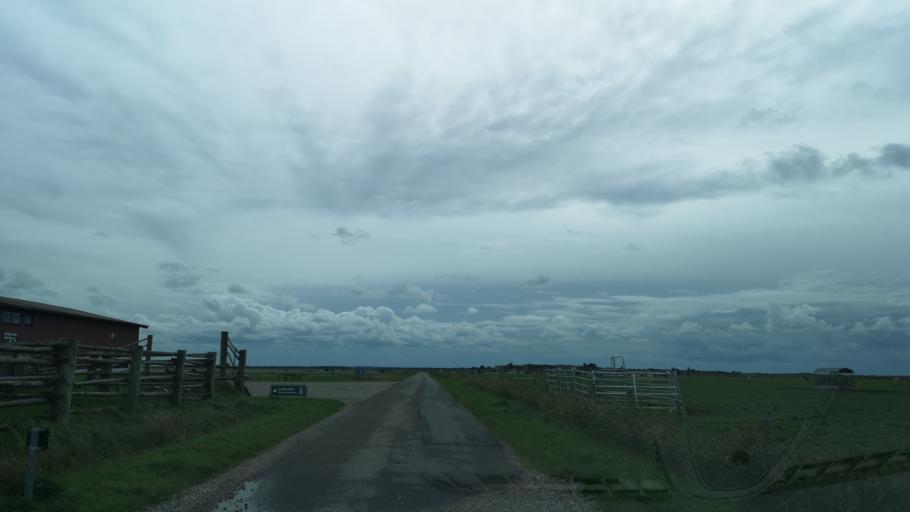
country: DK
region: Central Jutland
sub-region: Ringkobing-Skjern Kommune
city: Hvide Sande
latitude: 55.8622
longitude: 8.2202
